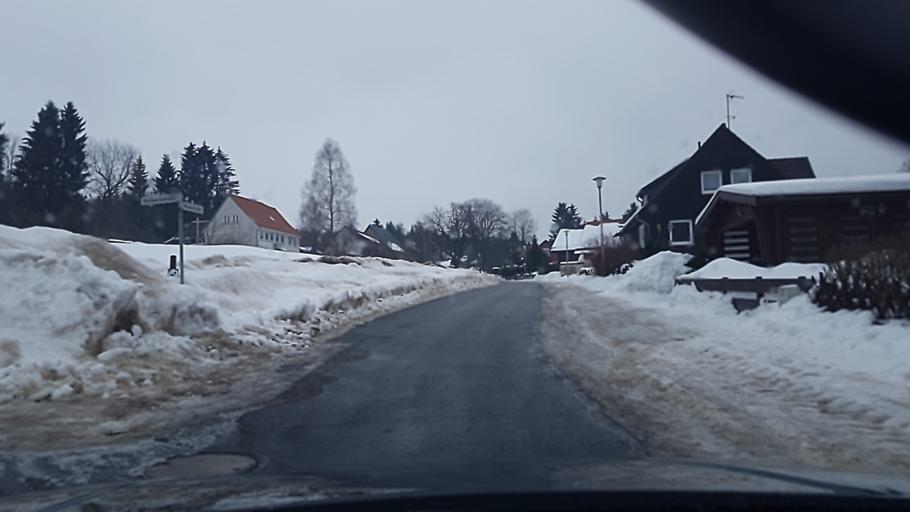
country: DE
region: Lower Saxony
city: Clausthal-Zellerfeld
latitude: 51.8489
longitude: 10.3332
